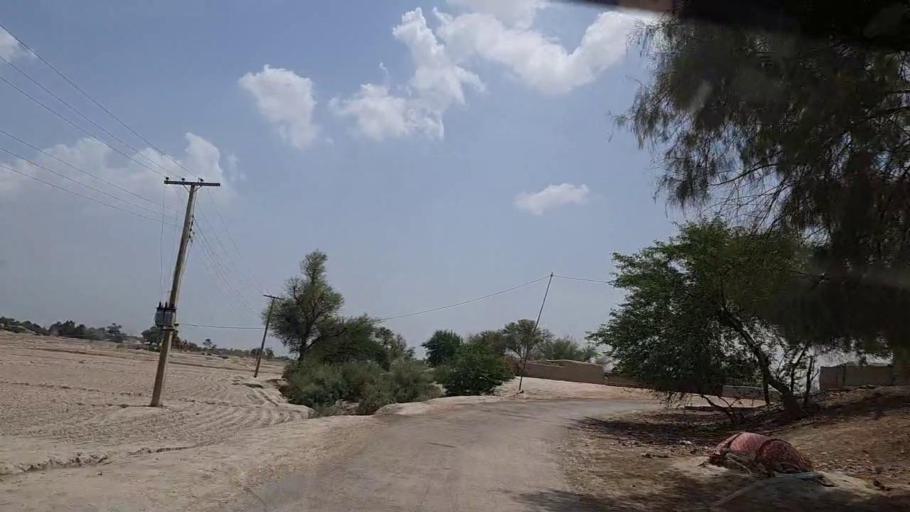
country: PK
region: Sindh
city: Bhan
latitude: 26.5416
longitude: 67.6349
